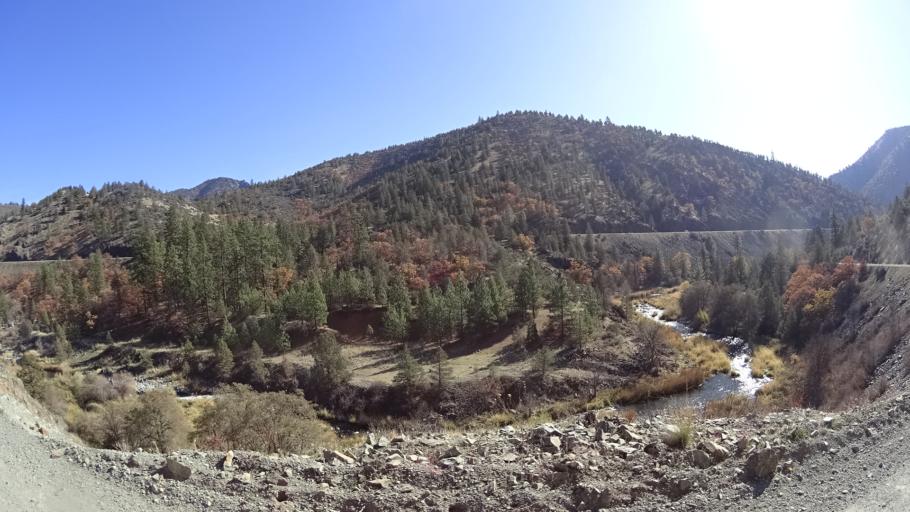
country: US
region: California
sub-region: Siskiyou County
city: Yreka
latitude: 41.7997
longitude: -122.6052
